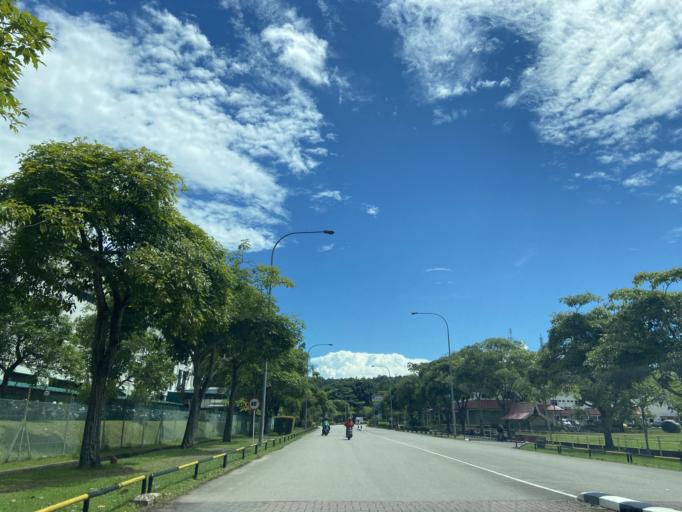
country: SG
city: Singapore
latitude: 1.0688
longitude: 104.0271
